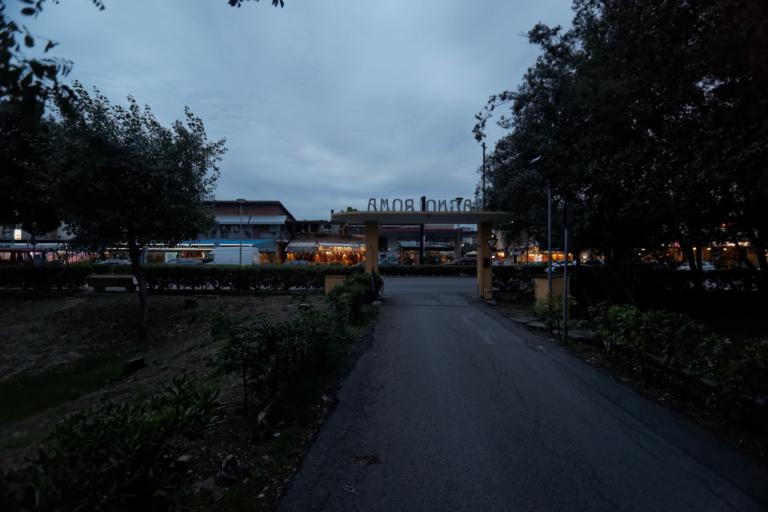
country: IT
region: Tuscany
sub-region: Province of Pisa
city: Marina di Pisa-Tirrenia-Calambrone
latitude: 43.6266
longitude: 10.2911
